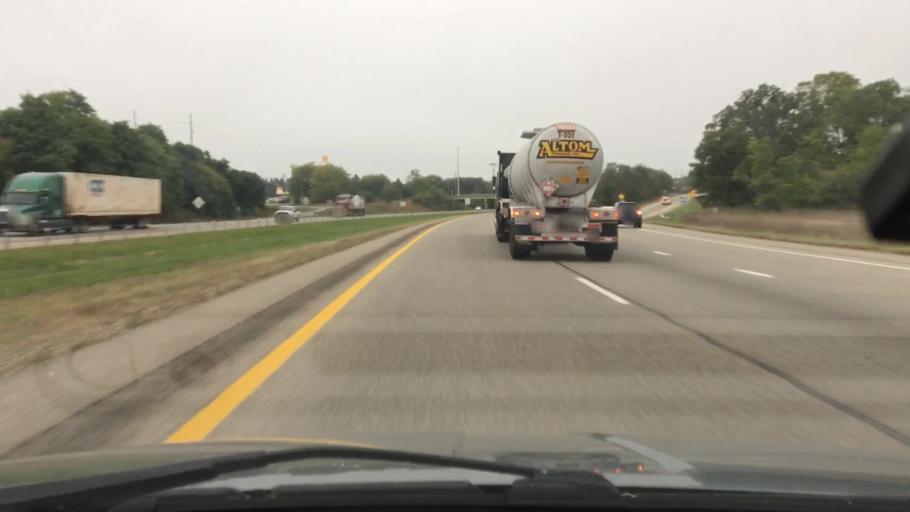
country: US
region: Michigan
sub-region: Calhoun County
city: Lakeview
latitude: 42.2623
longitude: -85.1929
